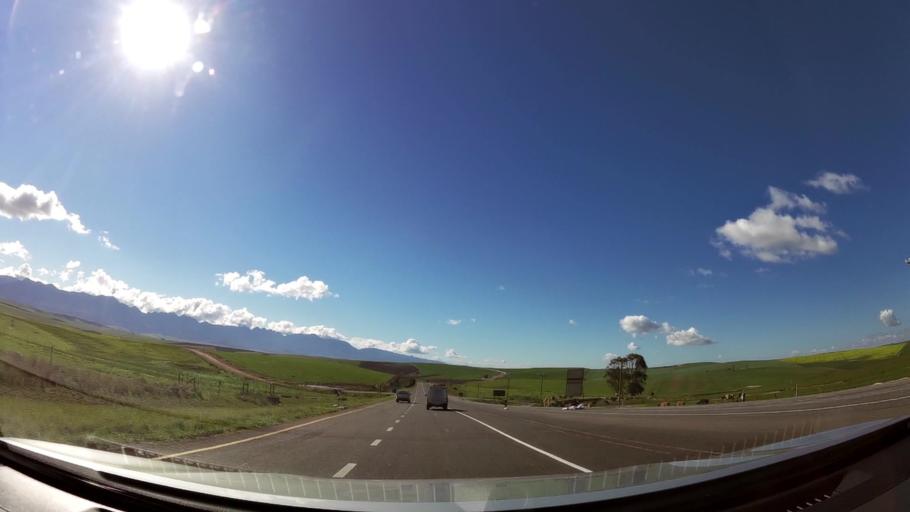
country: ZA
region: Western Cape
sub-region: Overberg District Municipality
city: Caledon
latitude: -34.2014
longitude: 19.6177
